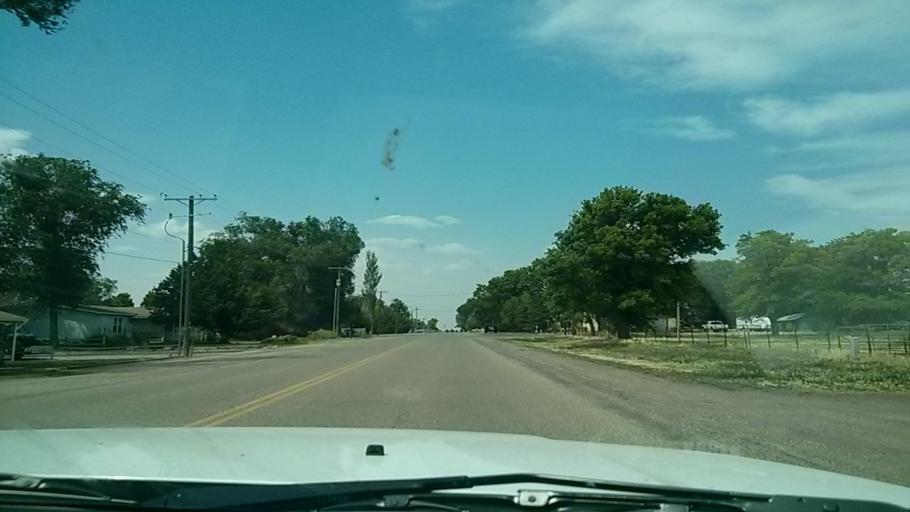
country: US
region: Utah
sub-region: Iron County
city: Cedar City
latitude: 37.5373
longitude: -113.1829
